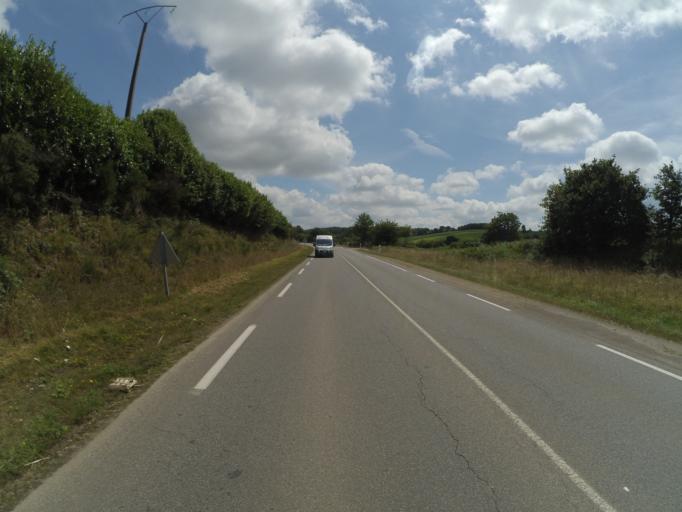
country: FR
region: Brittany
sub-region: Departement du Finistere
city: Elliant
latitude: 47.9686
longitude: -3.8969
